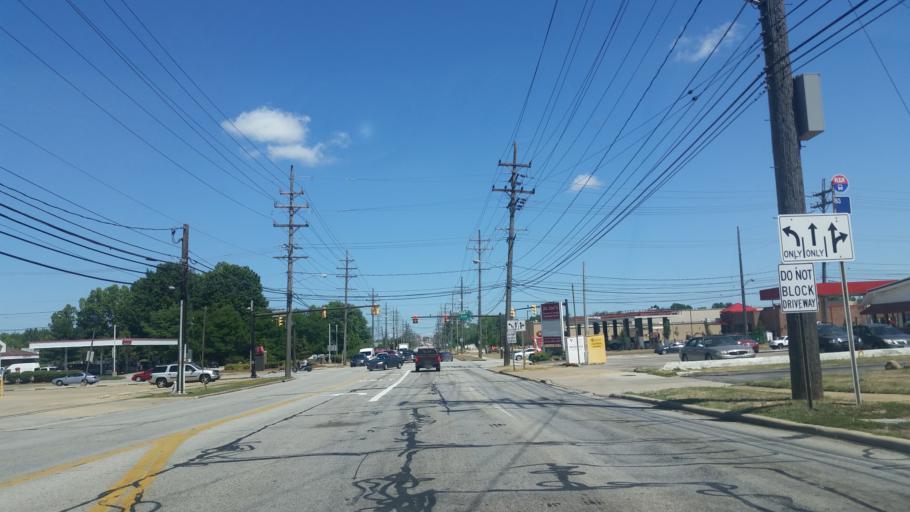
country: US
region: Ohio
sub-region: Cuyahoga County
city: Brook Park
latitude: 41.4043
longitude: -81.7841
